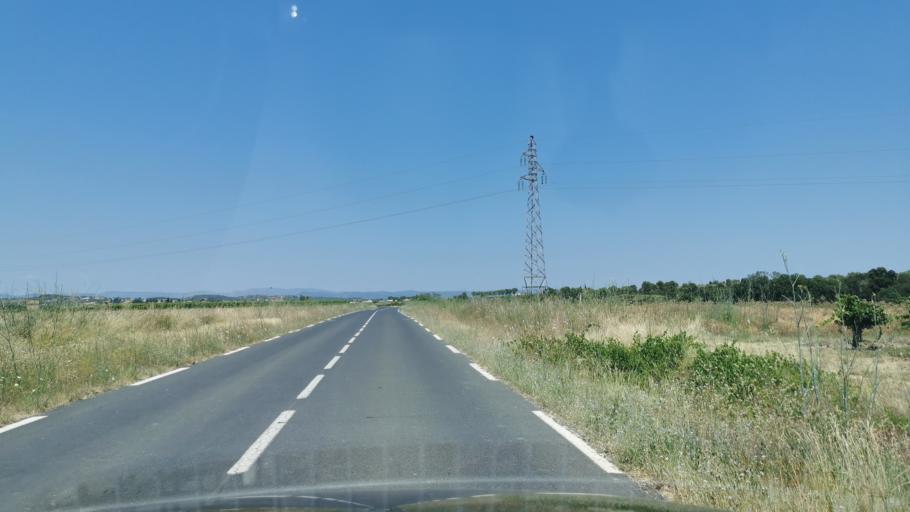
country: FR
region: Languedoc-Roussillon
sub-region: Departement de l'Herault
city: Maureilhan
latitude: 43.3714
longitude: 3.1135
